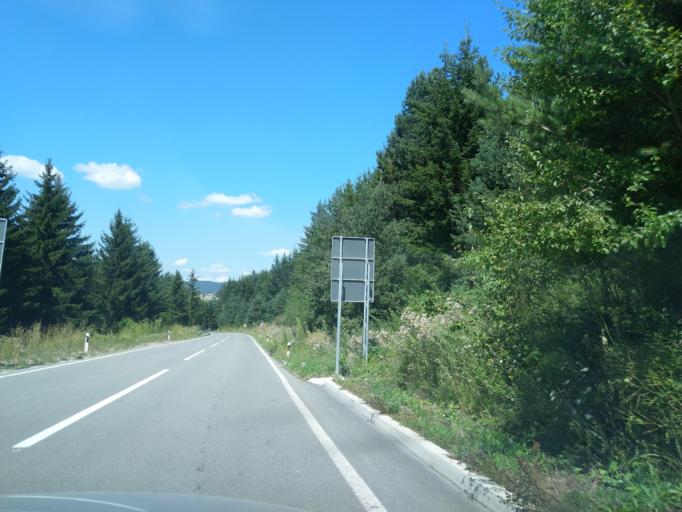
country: RS
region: Central Serbia
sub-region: Zlatiborski Okrug
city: Sjenica
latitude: 43.3147
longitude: 19.8928
